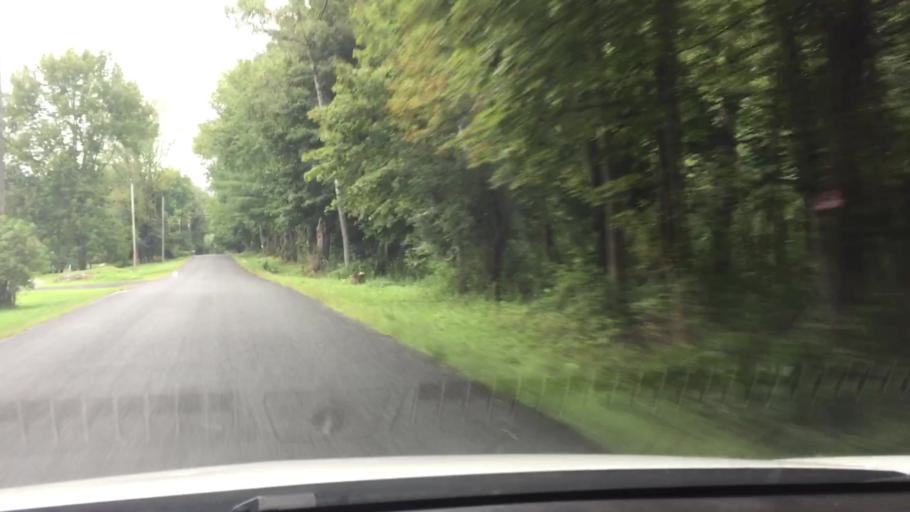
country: US
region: Massachusetts
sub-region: Berkshire County
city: Richmond
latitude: 42.3637
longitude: -73.3681
